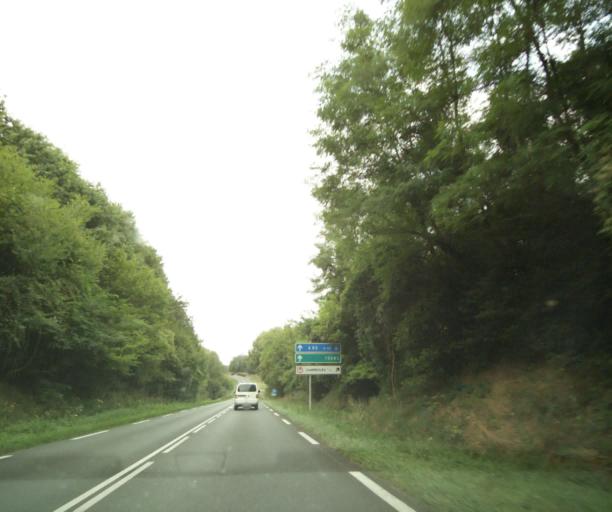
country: FR
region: Centre
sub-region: Departement d'Indre-et-Loire
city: Chambourg-sur-Indre
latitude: 47.1760
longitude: 0.9720
